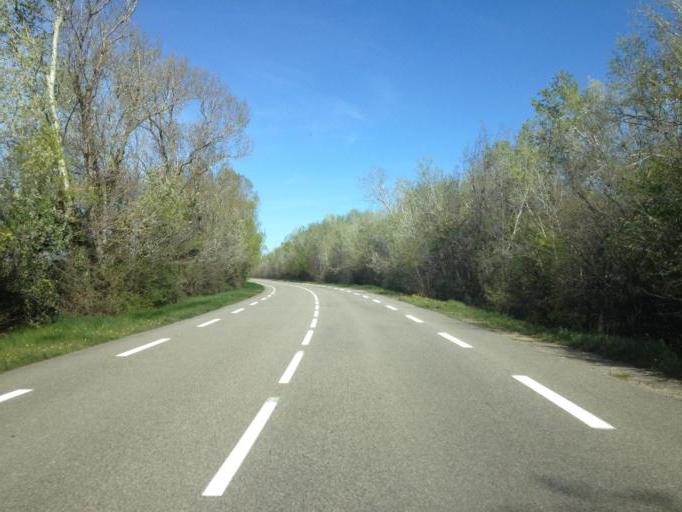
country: FR
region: Provence-Alpes-Cote d'Azur
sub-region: Departement du Vaucluse
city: Caderousse
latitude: 44.1112
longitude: 4.7267
